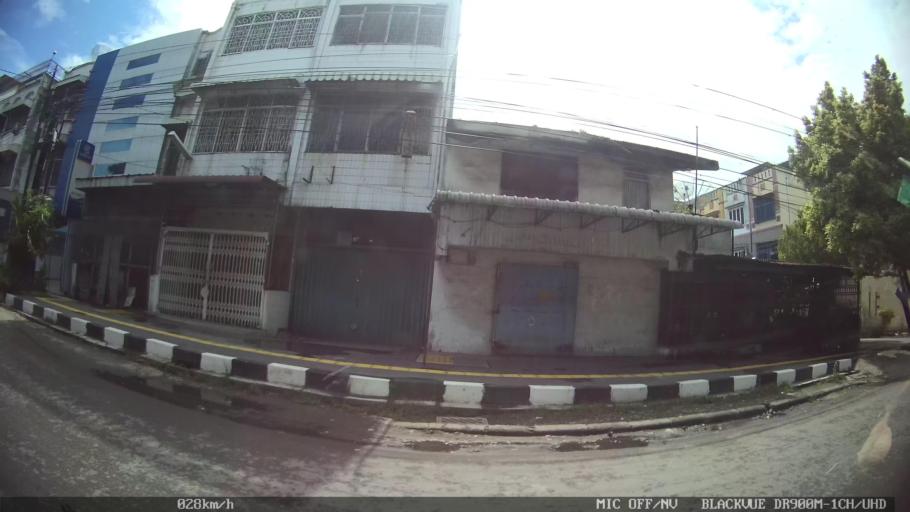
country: ID
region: North Sumatra
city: Medan
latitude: 3.5941
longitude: 98.7064
